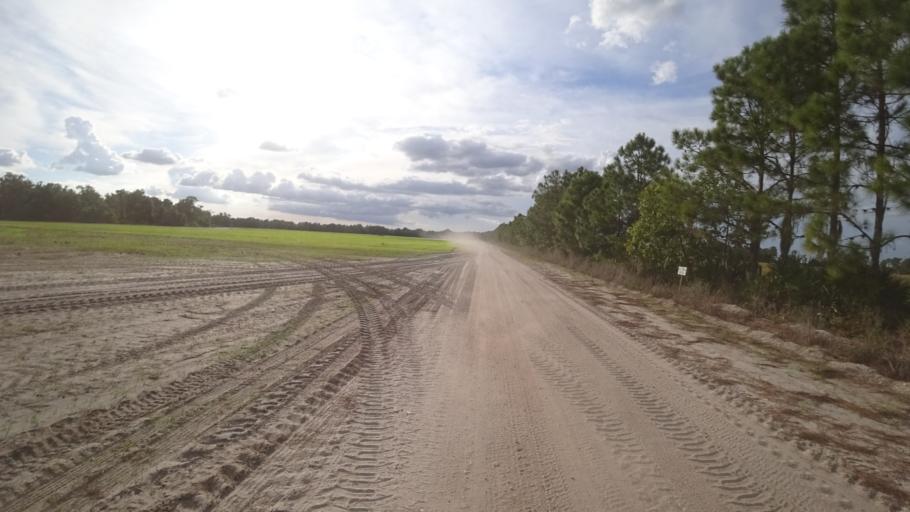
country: US
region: Florida
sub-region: Hillsborough County
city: Wimauma
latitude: 27.5664
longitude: -82.0848
